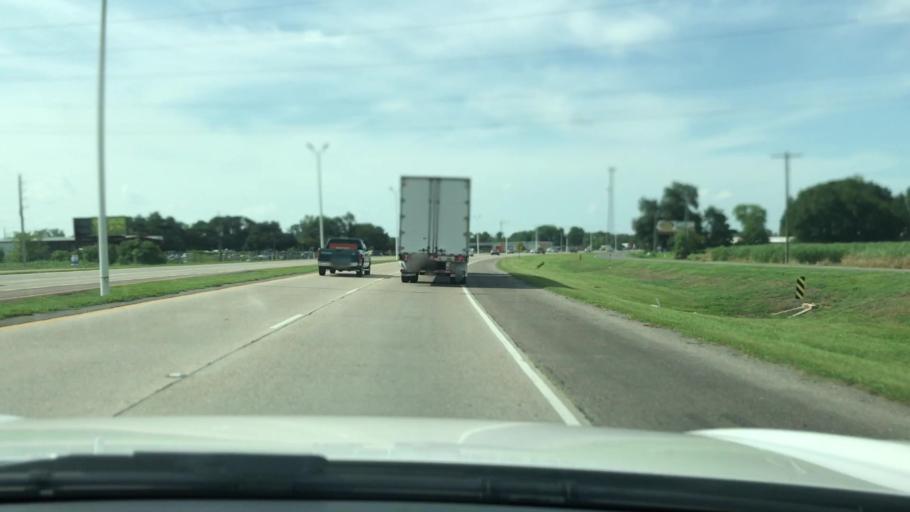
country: US
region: Louisiana
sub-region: West Baton Rouge Parish
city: Addis
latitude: 30.3608
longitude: -91.2608
